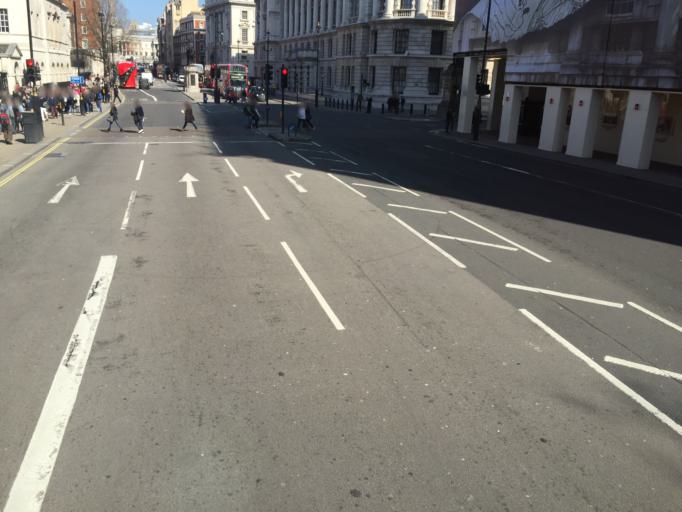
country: GB
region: England
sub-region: Greater London
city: London
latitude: 51.5043
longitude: -0.1263
